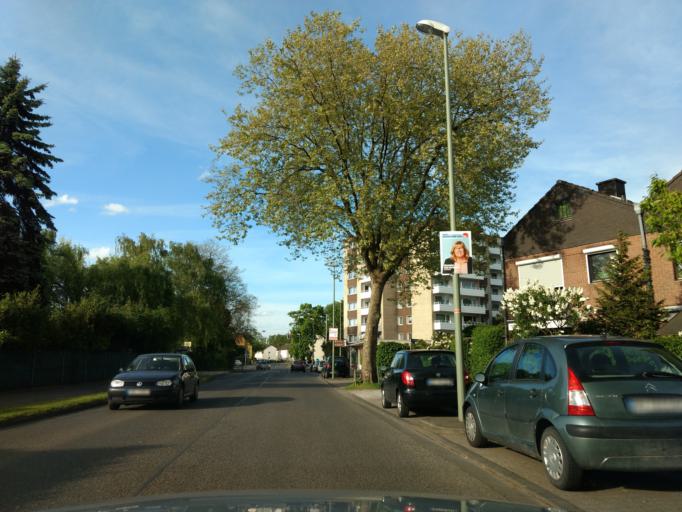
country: DE
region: North Rhine-Westphalia
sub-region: Regierungsbezirk Dusseldorf
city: Meerbusch
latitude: 51.2376
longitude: 6.6940
